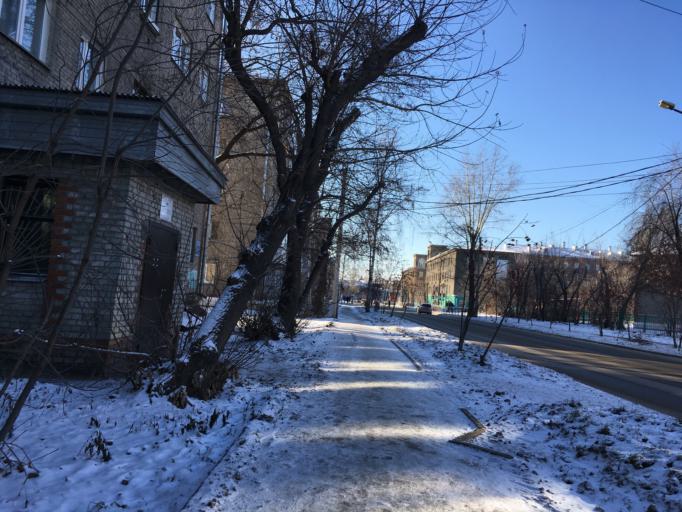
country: RU
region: Novosibirsk
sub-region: Novosibirskiy Rayon
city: Novosibirsk
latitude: 55.0546
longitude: 82.9659
